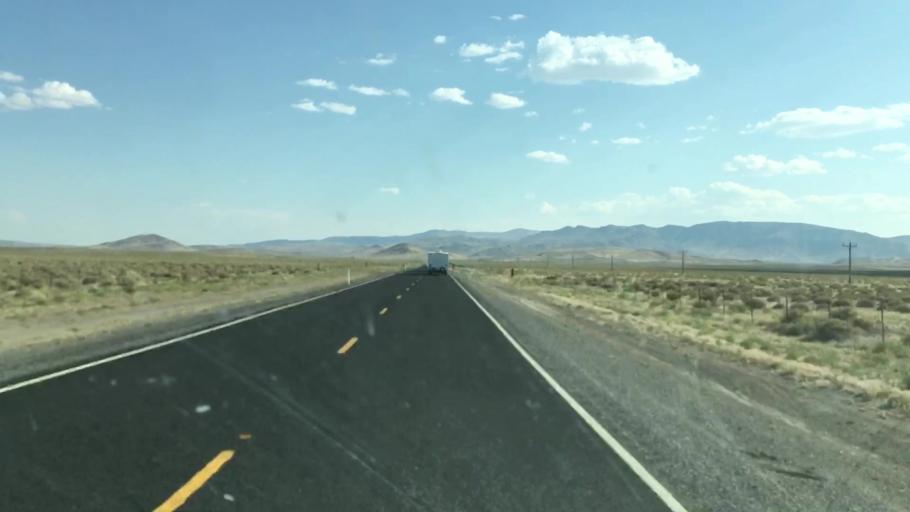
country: US
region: Nevada
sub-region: Lyon County
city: Fernley
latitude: 39.6738
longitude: -119.3328
